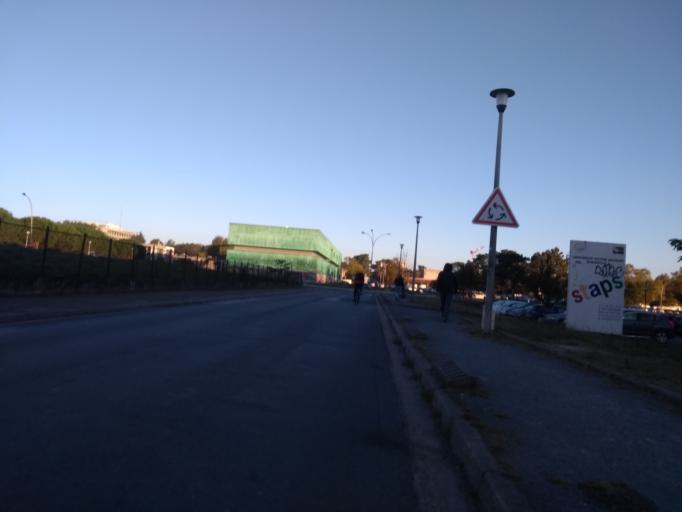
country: FR
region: Aquitaine
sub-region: Departement de la Gironde
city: Gradignan
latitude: 44.7934
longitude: -0.6152
